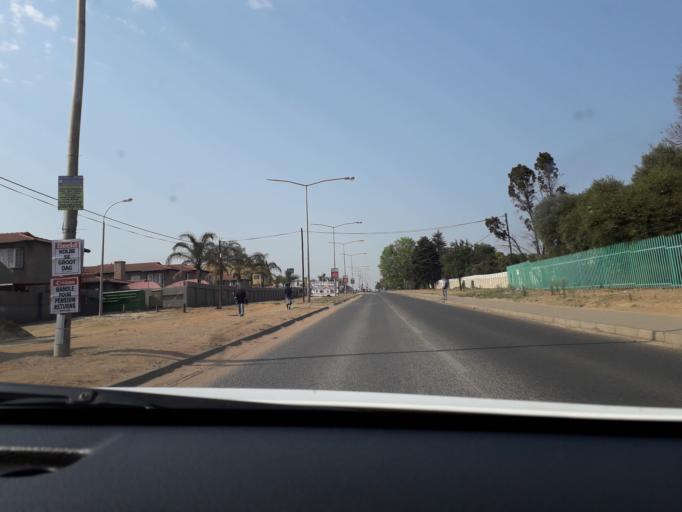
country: ZA
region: Gauteng
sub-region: Ekurhuleni Metropolitan Municipality
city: Tembisa
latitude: -26.0749
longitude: 28.2474
